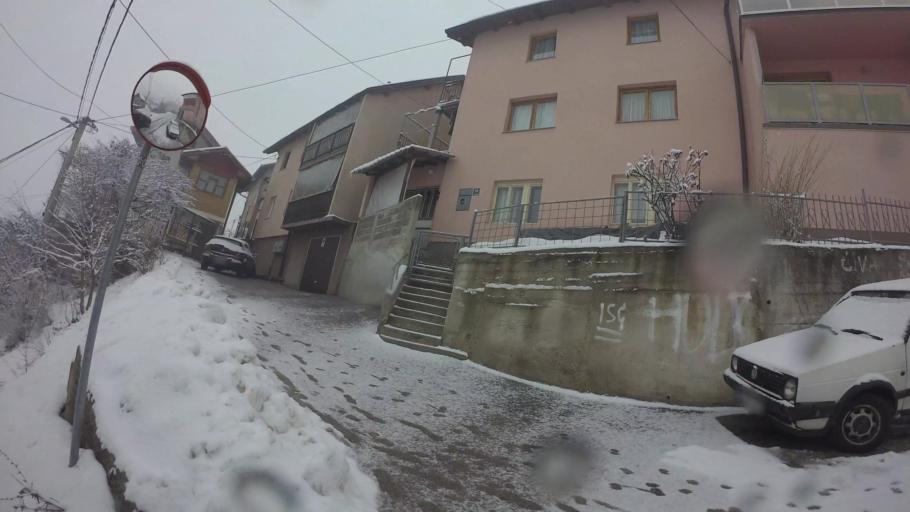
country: BA
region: Federation of Bosnia and Herzegovina
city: Kobilja Glava
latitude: 43.8463
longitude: 18.4280
